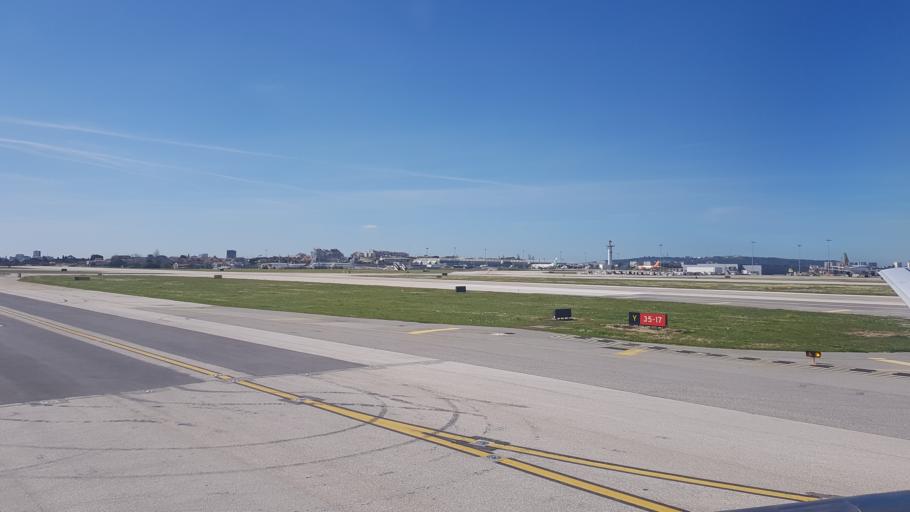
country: PT
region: Lisbon
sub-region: Loures
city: Moscavide
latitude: 38.7702
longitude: -9.1316
